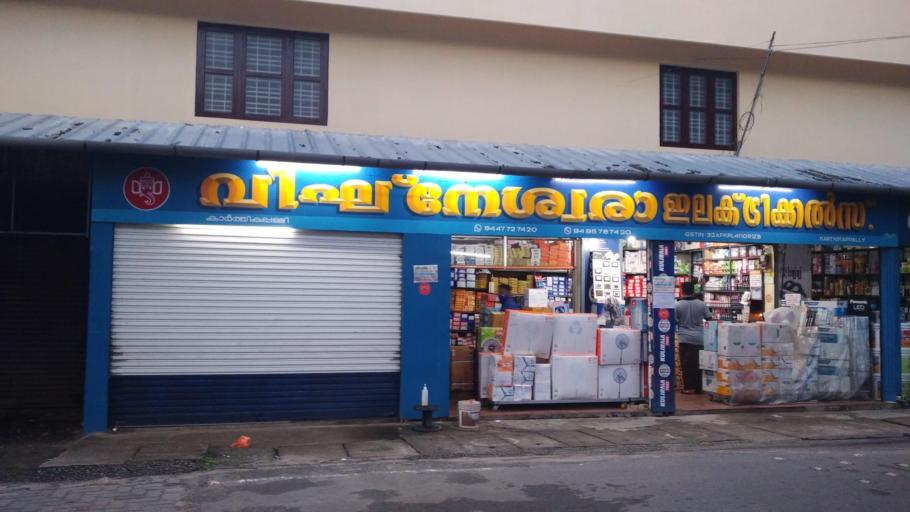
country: IN
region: Kerala
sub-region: Alappuzha
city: Kayankulam
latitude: 9.2588
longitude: 76.4501
